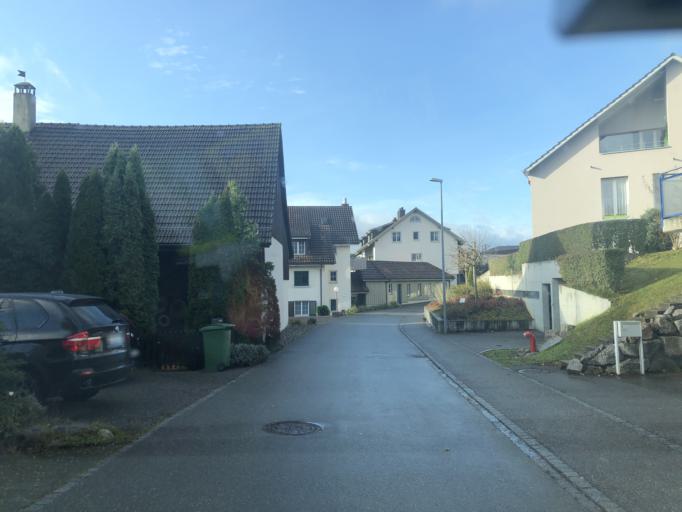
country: CH
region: Aargau
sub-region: Bezirk Baden
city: Unterehrendingen
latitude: 47.5227
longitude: 8.3592
